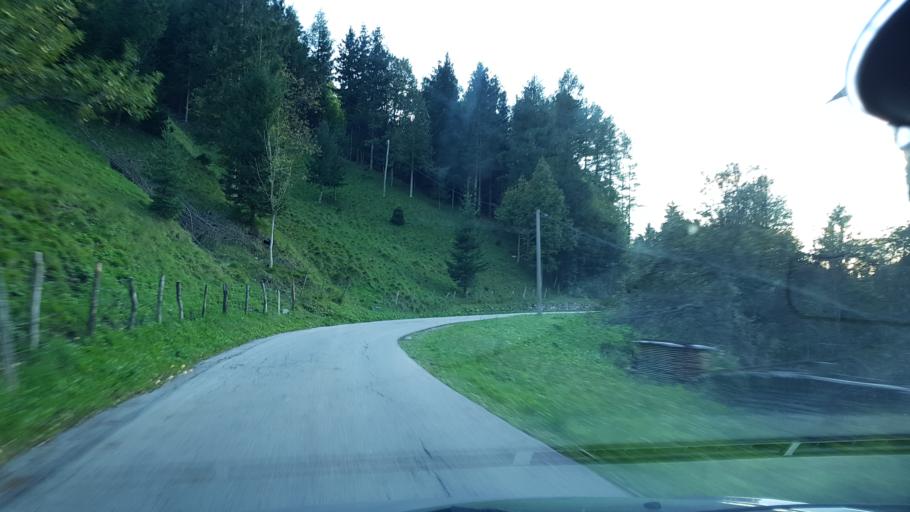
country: SI
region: Kobarid
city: Kobarid
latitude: 46.2665
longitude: 13.6104
